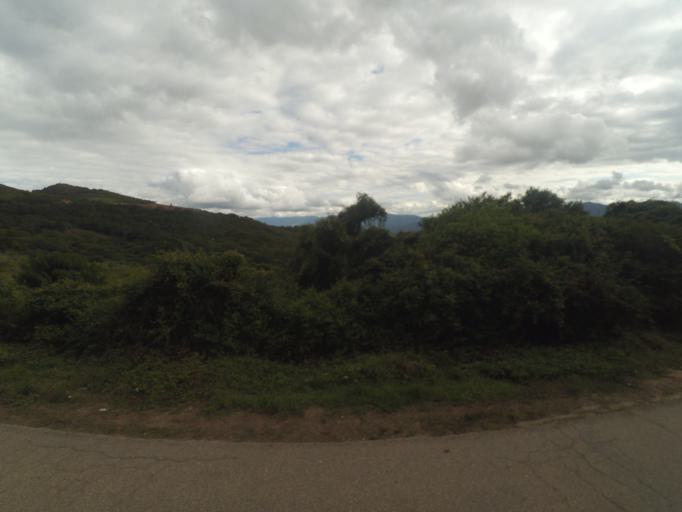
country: BO
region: Santa Cruz
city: Samaipata
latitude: -18.1771
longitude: -63.8654
